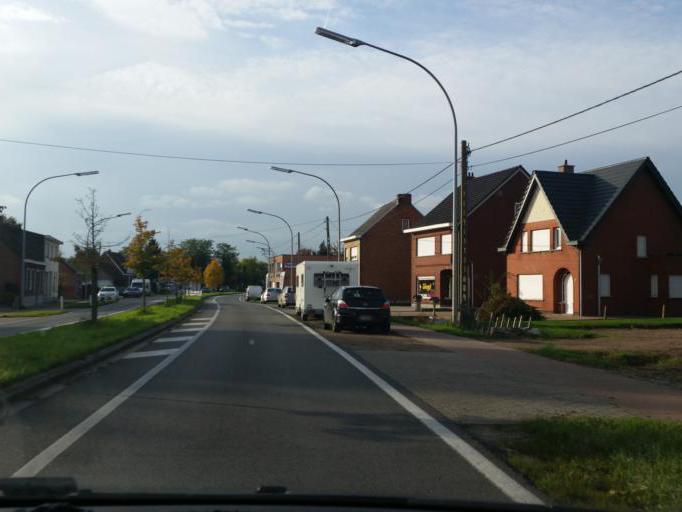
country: BE
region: Flanders
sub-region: Provincie Antwerpen
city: Berlaar
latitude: 51.0862
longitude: 4.6459
